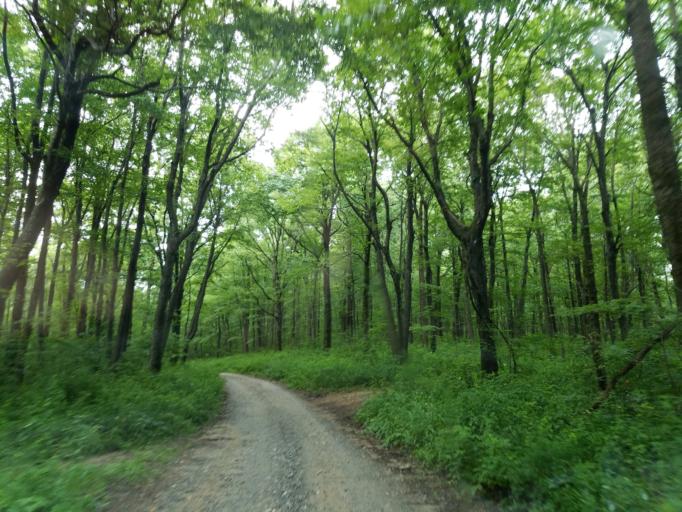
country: US
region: Georgia
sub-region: Lumpkin County
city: Dahlonega
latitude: 34.6472
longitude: -84.1456
